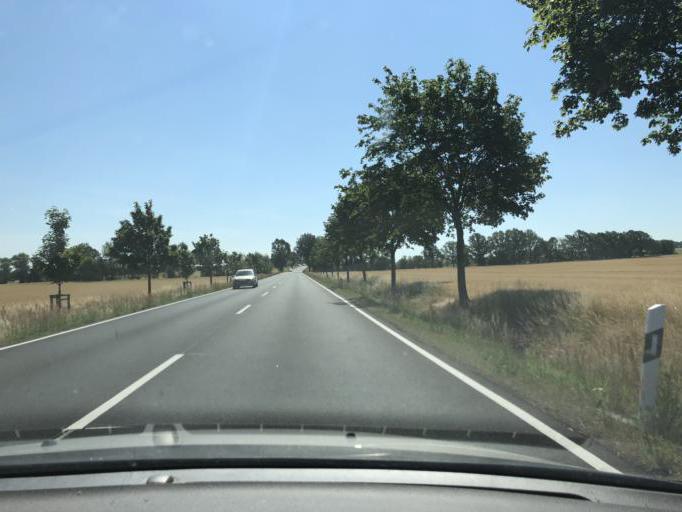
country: DE
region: Saxony
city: Oschatz
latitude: 51.3220
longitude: 13.0505
